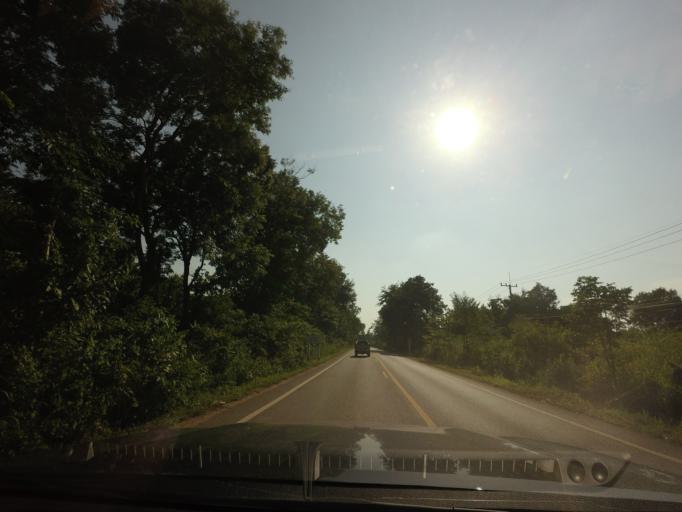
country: TH
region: Nan
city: Nan
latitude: 18.8110
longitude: 100.8026
